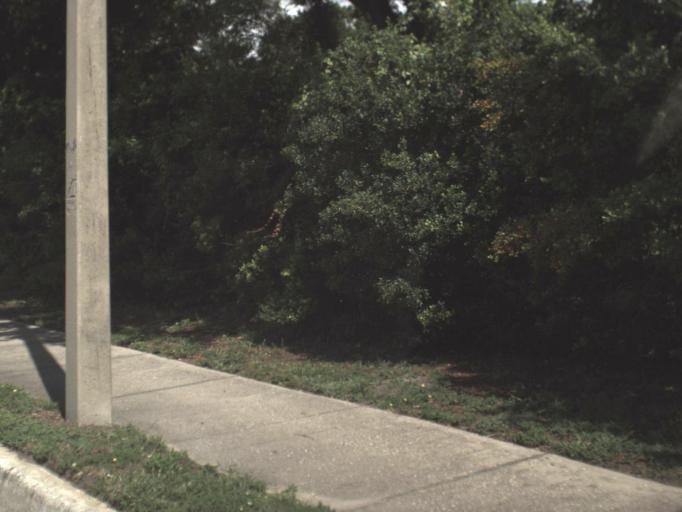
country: US
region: Florida
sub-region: Hillsborough County
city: Egypt Lake-Leto
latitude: 27.9815
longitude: -82.5023
